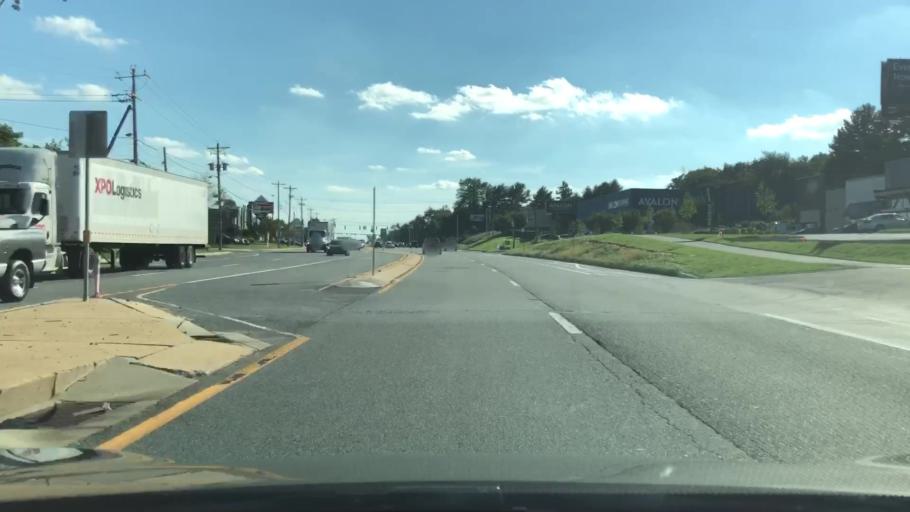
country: US
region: Delaware
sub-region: New Castle County
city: Bellefonte
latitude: 39.8348
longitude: -75.5426
